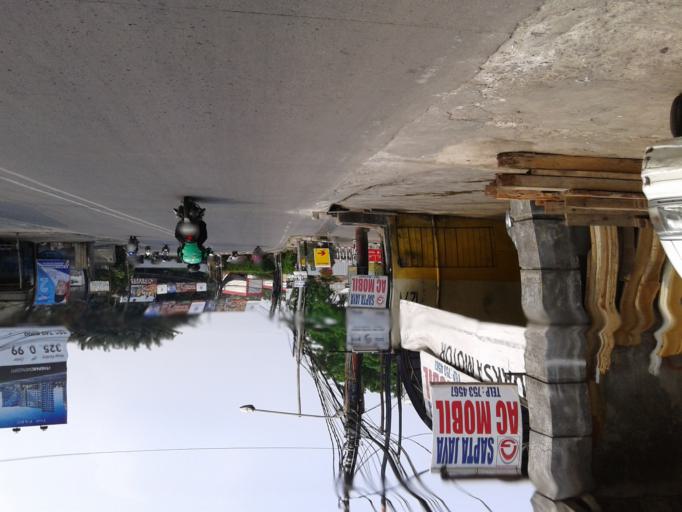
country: ID
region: West Java
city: Pamulang
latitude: -6.3274
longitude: 106.7851
